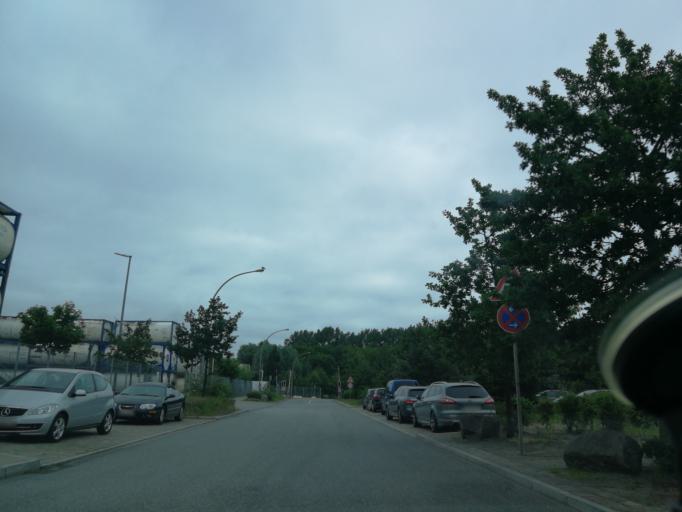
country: DE
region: Hamburg
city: Altona
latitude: 53.5085
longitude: 9.9255
